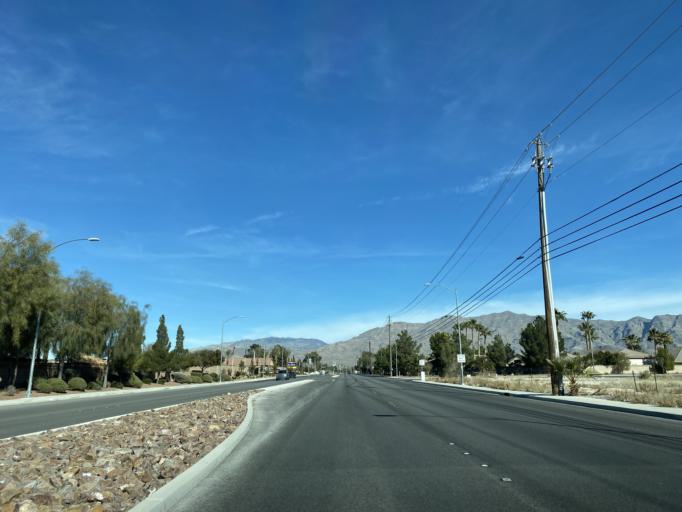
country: US
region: Nevada
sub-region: Clark County
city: North Las Vegas
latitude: 36.2933
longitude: -115.2241
